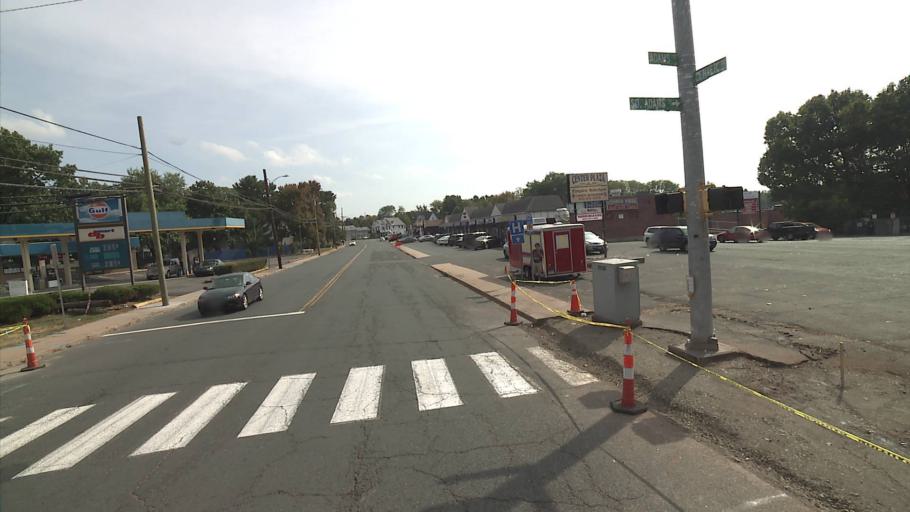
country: US
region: Connecticut
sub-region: Hartford County
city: Manchester
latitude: 41.7753
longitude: -72.5490
